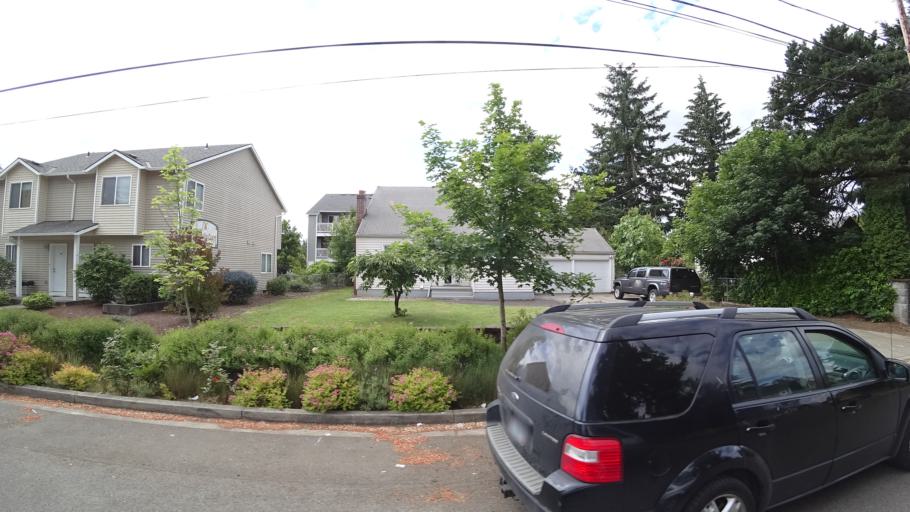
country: US
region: Oregon
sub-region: Multnomah County
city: Lents
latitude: 45.4954
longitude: -122.5248
